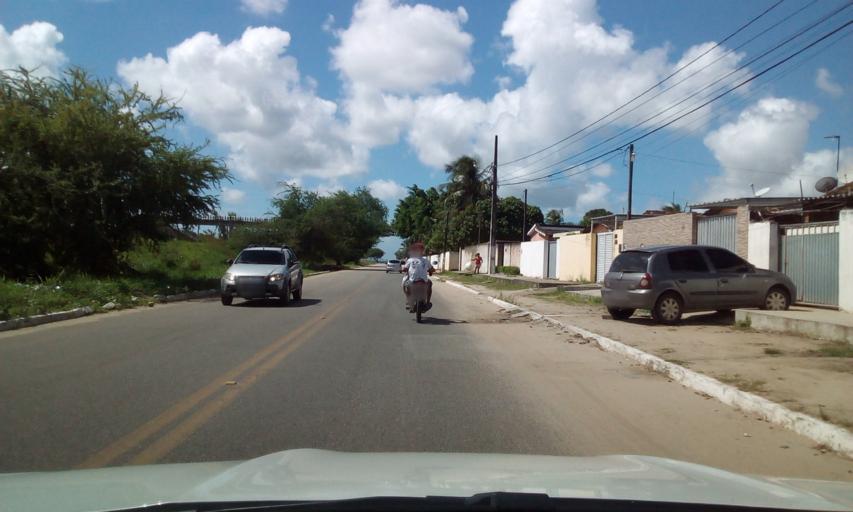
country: BR
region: Paraiba
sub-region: Bayeux
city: Bayeux
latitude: -7.1289
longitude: -34.9524
